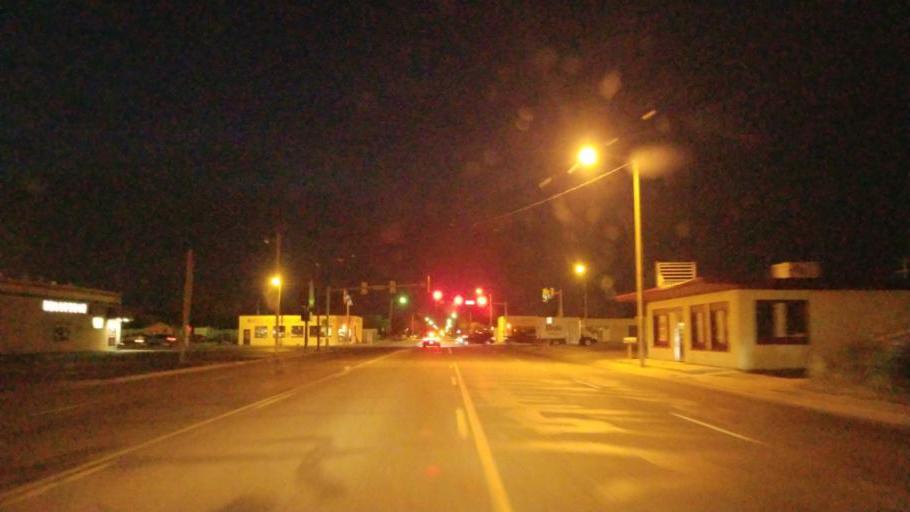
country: US
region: Texas
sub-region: Potter County
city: Amarillo
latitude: 35.2010
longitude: -101.8255
